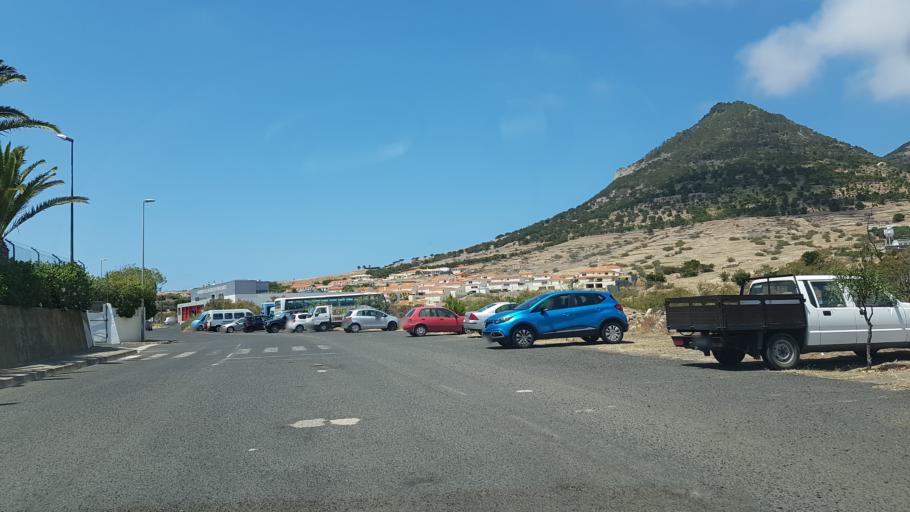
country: PT
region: Madeira
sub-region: Porto Santo
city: Vila de Porto Santo
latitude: 33.0698
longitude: -16.3423
